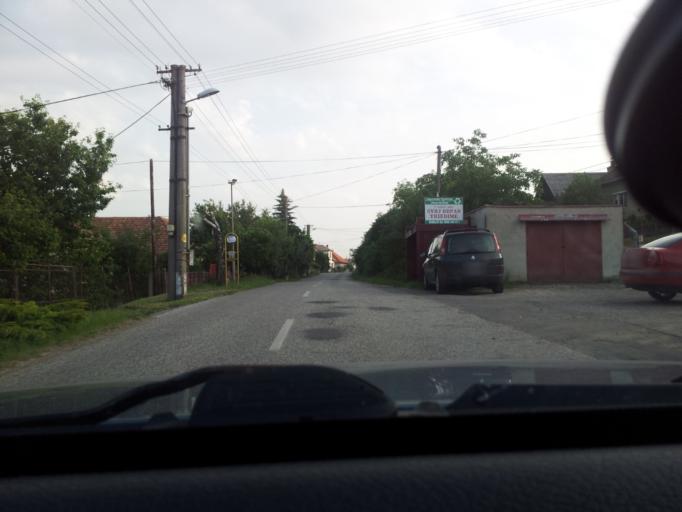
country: SK
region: Banskobystricky
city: Nova Bana
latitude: 48.3609
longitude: 18.7275
